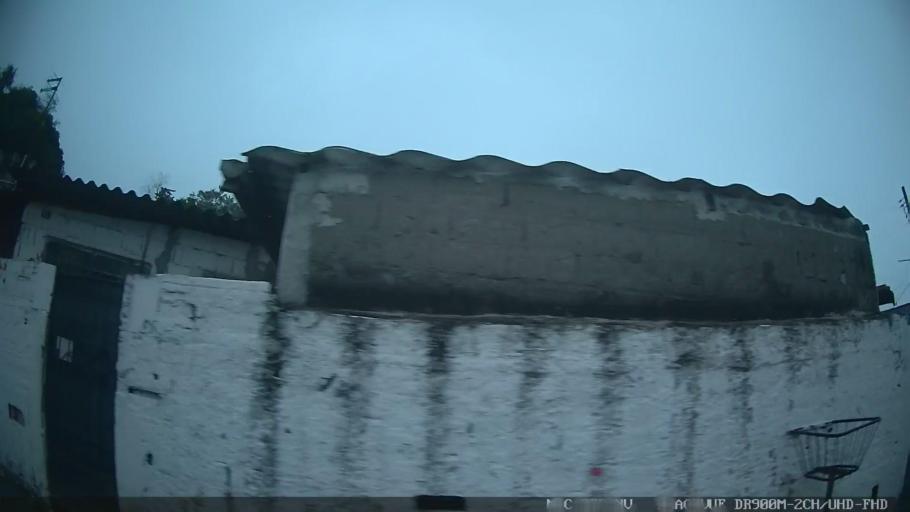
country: BR
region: Sao Paulo
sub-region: Mogi das Cruzes
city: Mogi das Cruzes
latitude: -23.5050
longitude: -46.2161
